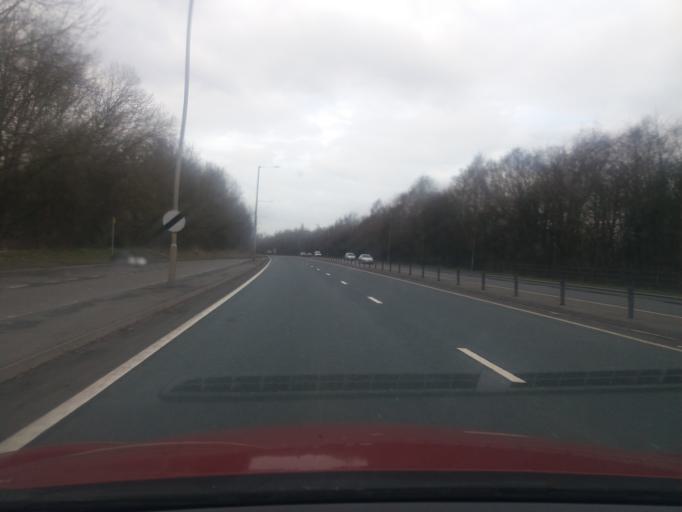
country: GB
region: England
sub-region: Lancashire
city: Leyland
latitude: 53.7384
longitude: -2.6787
